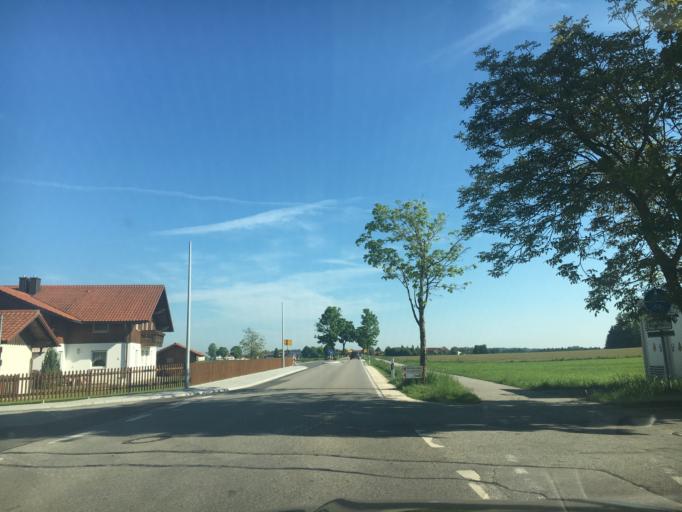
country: DE
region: Bavaria
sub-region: Upper Bavaria
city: Tacherting
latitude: 48.0823
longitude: 12.5956
